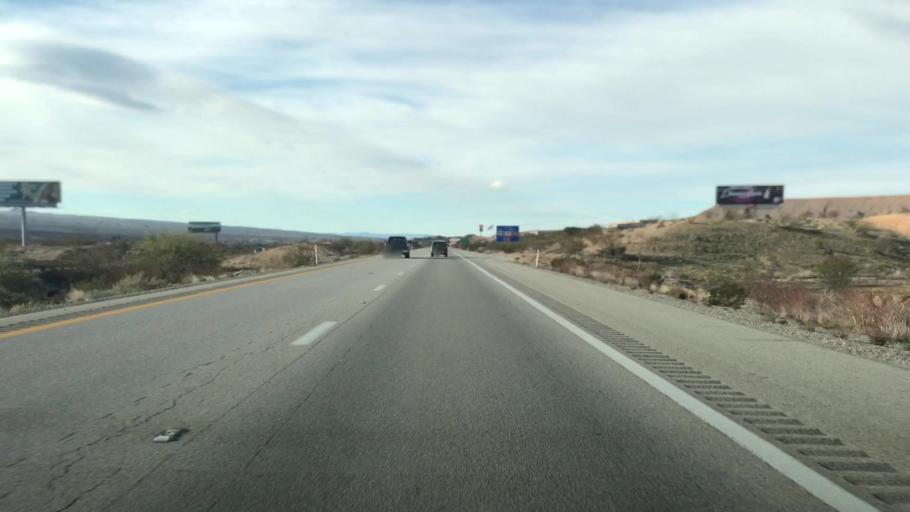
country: US
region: Nevada
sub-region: Clark County
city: Bunkerville
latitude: 36.7934
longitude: -114.1229
